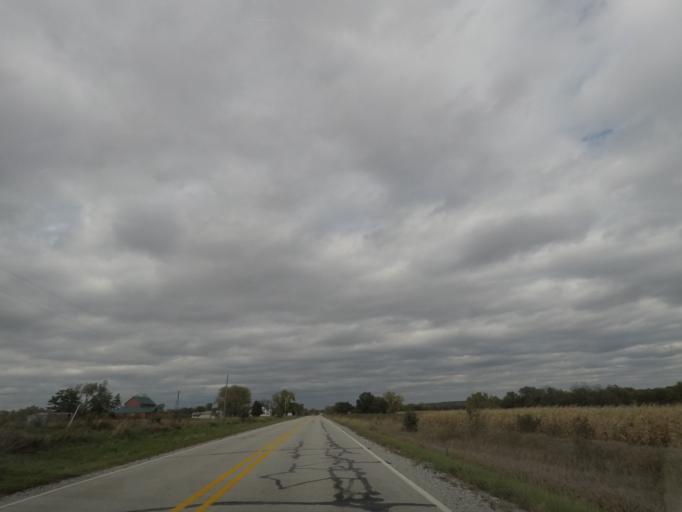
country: US
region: Iowa
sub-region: Story County
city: Huxley
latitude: 41.8598
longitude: -93.5316
